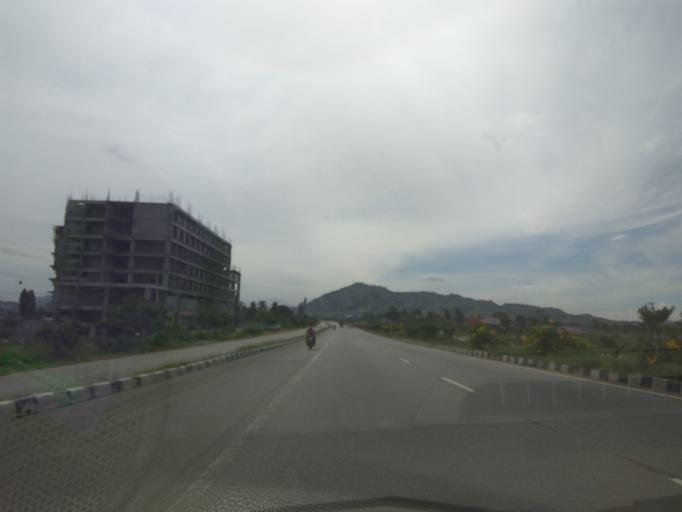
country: IN
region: Karnataka
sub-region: Kolar
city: Malur
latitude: 13.1306
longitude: 77.9875
